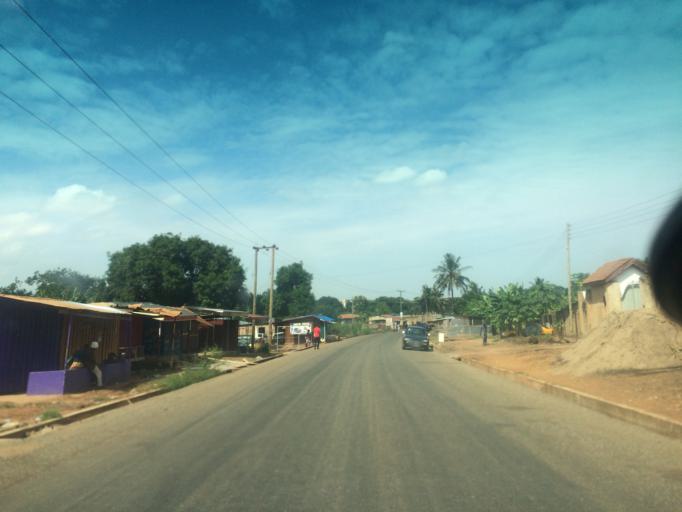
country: GH
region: Greater Accra
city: Medina Estates
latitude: 5.7425
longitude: -0.1756
